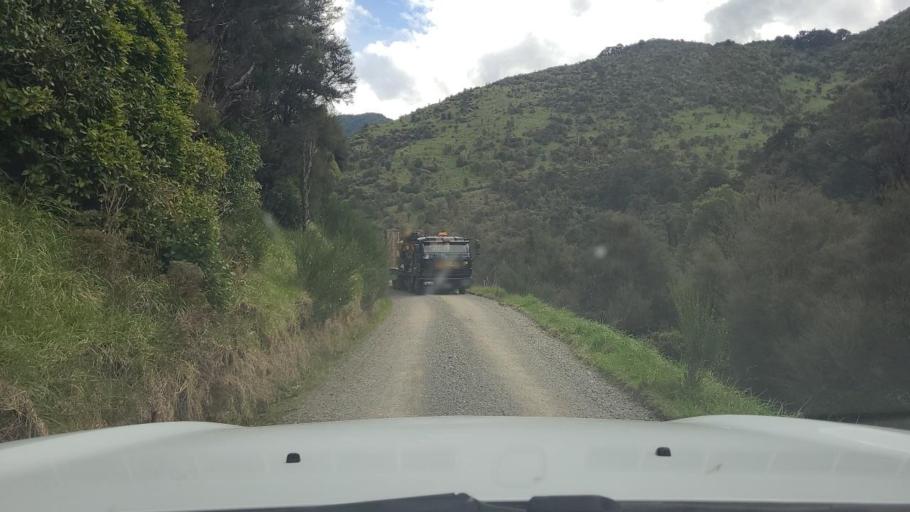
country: NZ
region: Wellington
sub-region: Masterton District
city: Masterton
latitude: -40.9333
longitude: 175.4832
